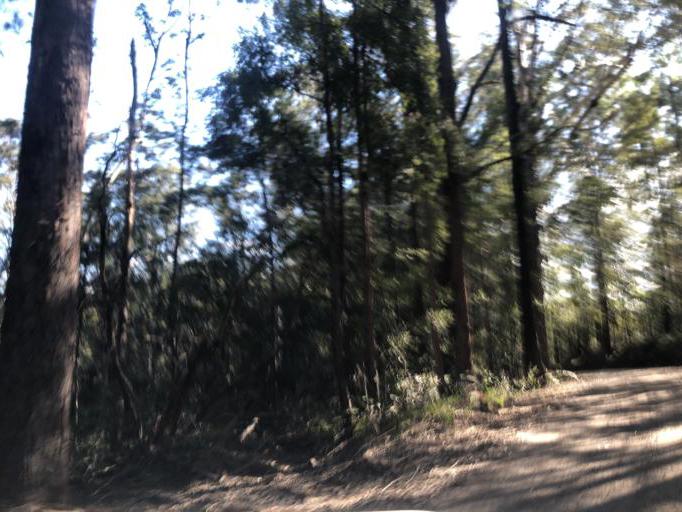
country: AU
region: New South Wales
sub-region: Bellingen
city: Bellingen
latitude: -30.4339
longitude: 152.8368
